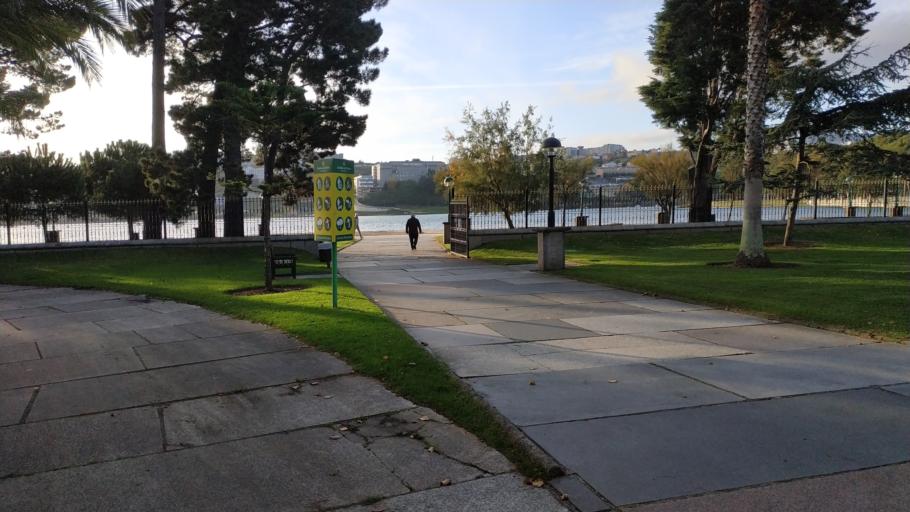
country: ES
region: Galicia
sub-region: Provincia da Coruna
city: A Coruna
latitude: 43.3372
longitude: -8.3792
